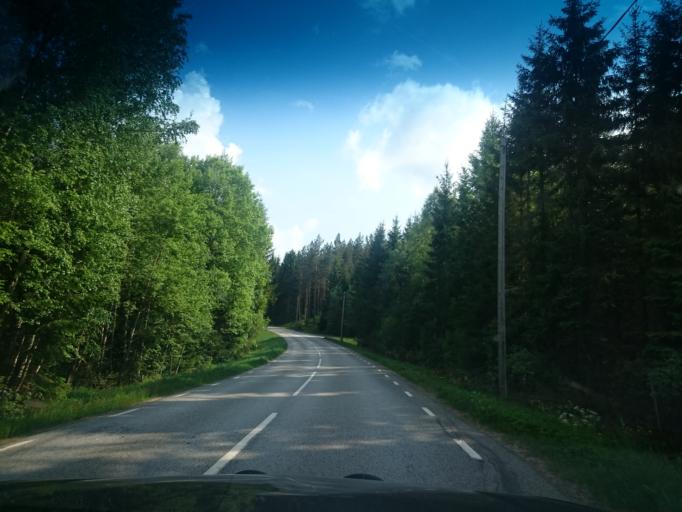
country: SE
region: Joenkoeping
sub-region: Vetlanda Kommun
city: Vetlanda
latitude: 57.3368
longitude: 15.0759
